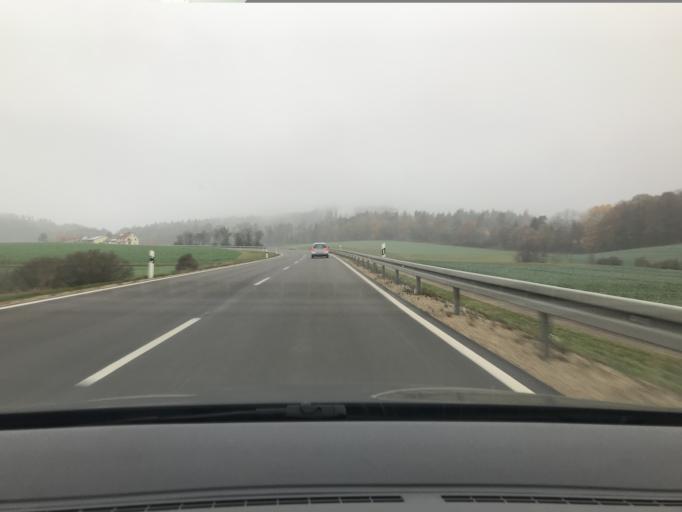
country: DE
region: Bavaria
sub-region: Swabia
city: Fremdingen
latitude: 48.9852
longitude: 10.4336
